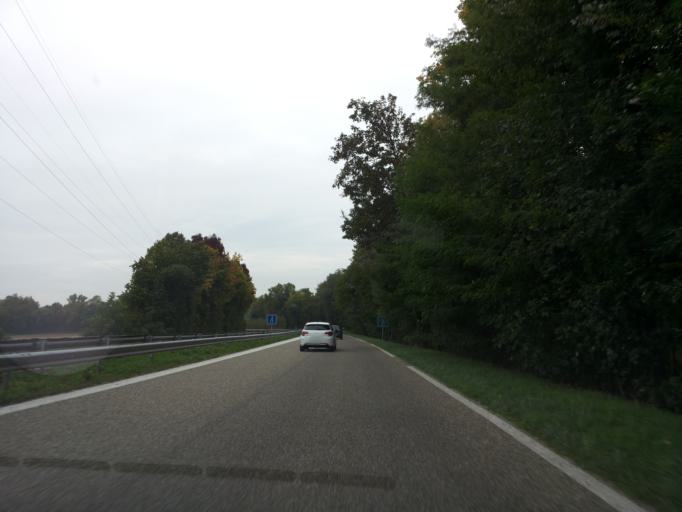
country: FR
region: Alsace
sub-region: Departement du Bas-Rhin
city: Illkirch-Graffenstaden
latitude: 48.5149
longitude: 7.7285
